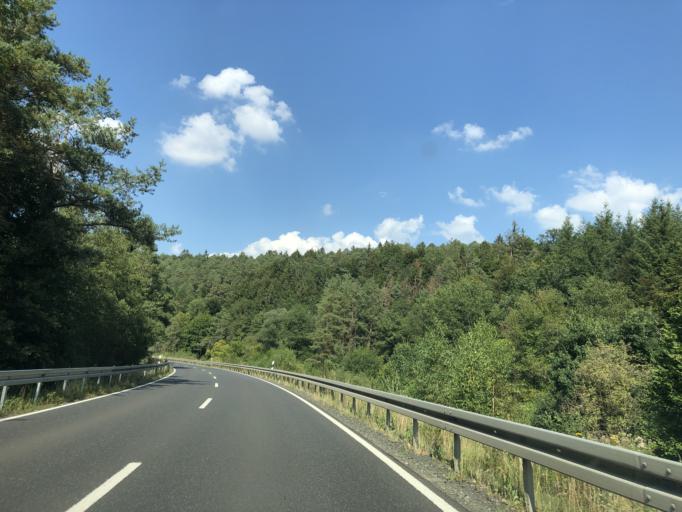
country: DE
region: Hesse
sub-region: Regierungsbezirk Giessen
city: Kirchhain
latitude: 50.8525
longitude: 8.9349
